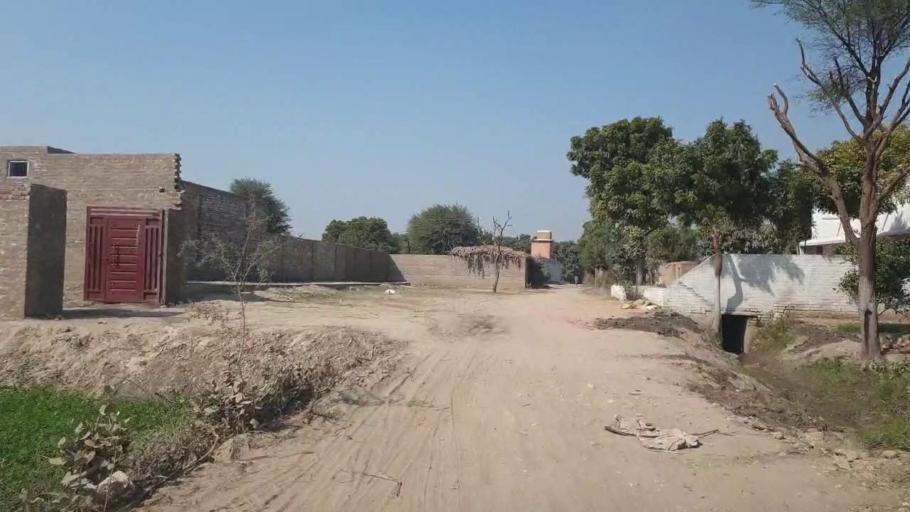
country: PK
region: Sindh
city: Tando Jam
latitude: 25.3305
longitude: 68.5950
